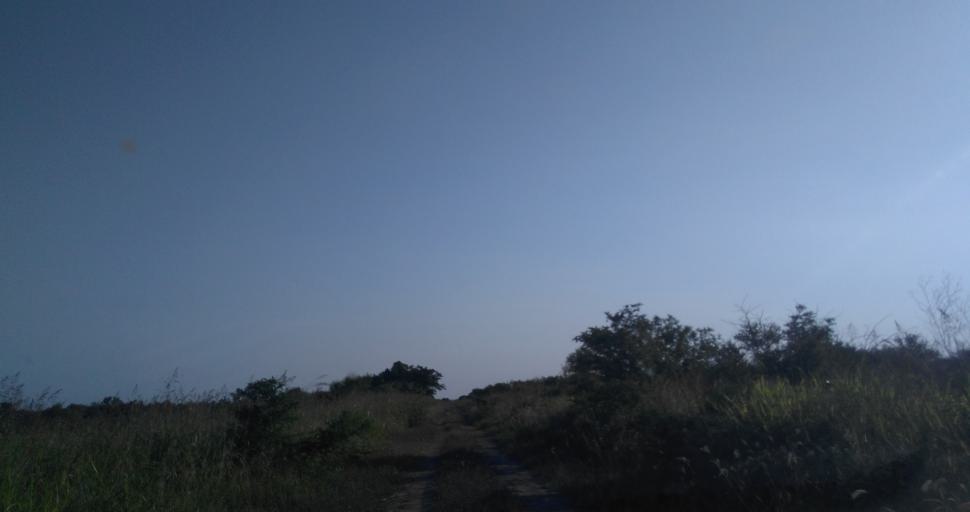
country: AR
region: Chaco
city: Fontana
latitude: -27.4320
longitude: -59.0596
